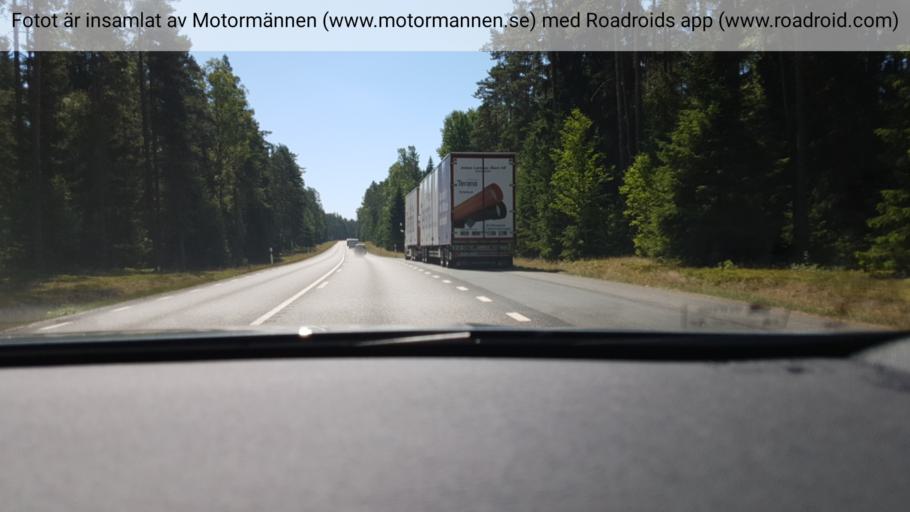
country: SE
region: Joenkoeping
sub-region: Gnosjo Kommun
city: Gnosjoe
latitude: 57.5078
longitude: 13.6766
